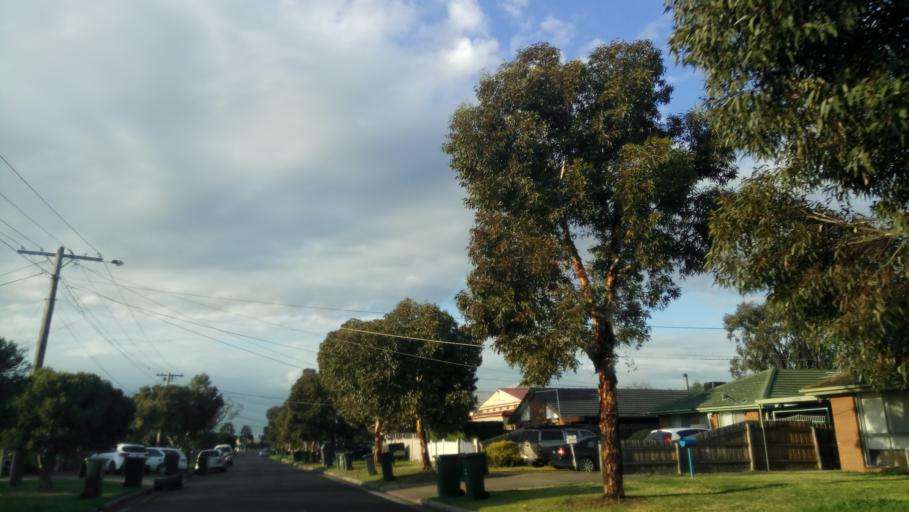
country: AU
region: Victoria
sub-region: Hobsons Bay
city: Laverton
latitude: -37.8688
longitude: 144.7757
